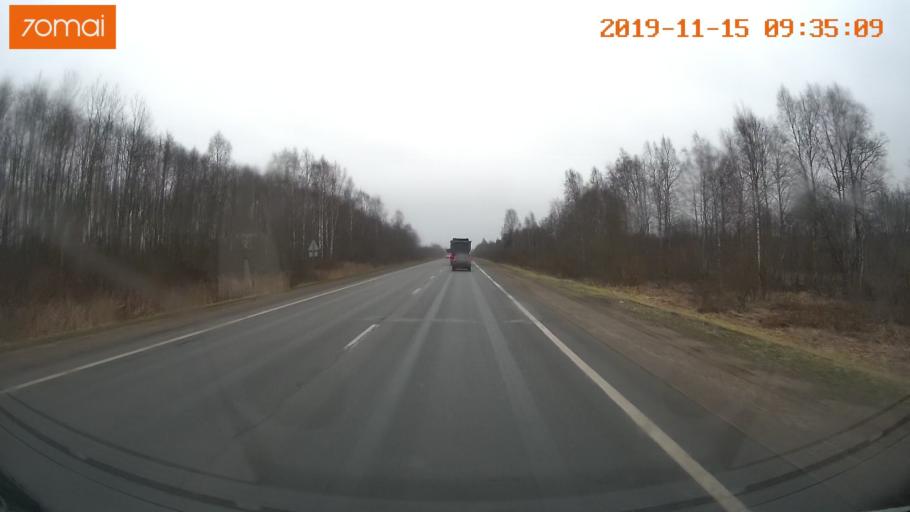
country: RU
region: Vologda
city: Sheksna
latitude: 59.2559
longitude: 38.3936
